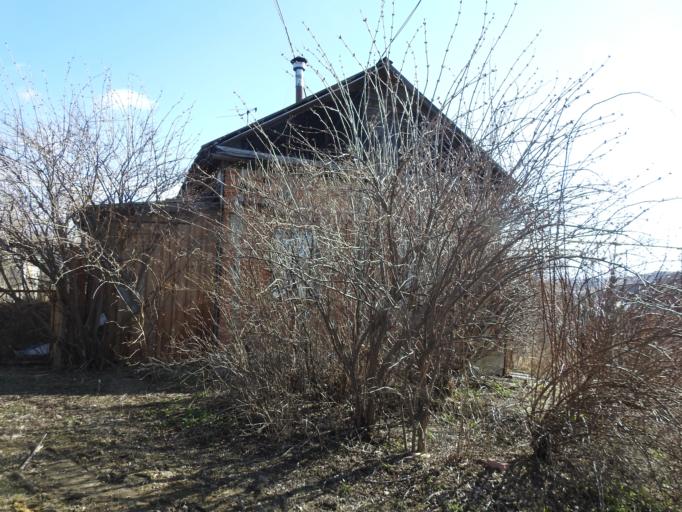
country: RU
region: Saratov
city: Krasnyy Oktyabr'
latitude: 51.3836
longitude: 45.7402
